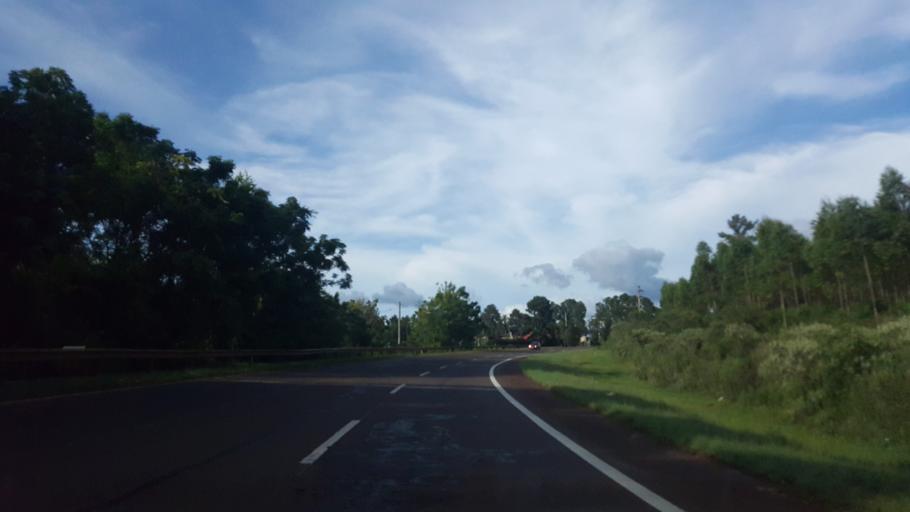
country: AR
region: Misiones
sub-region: Departamento de San Ignacio
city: San Ignacio
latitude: -27.2699
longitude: -55.5402
